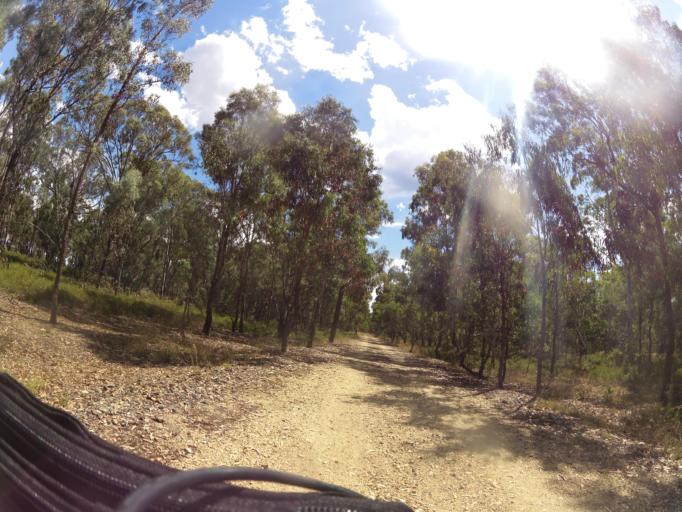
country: AU
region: Victoria
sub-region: Wellington
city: Heyfield
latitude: -37.9828
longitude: 146.7283
